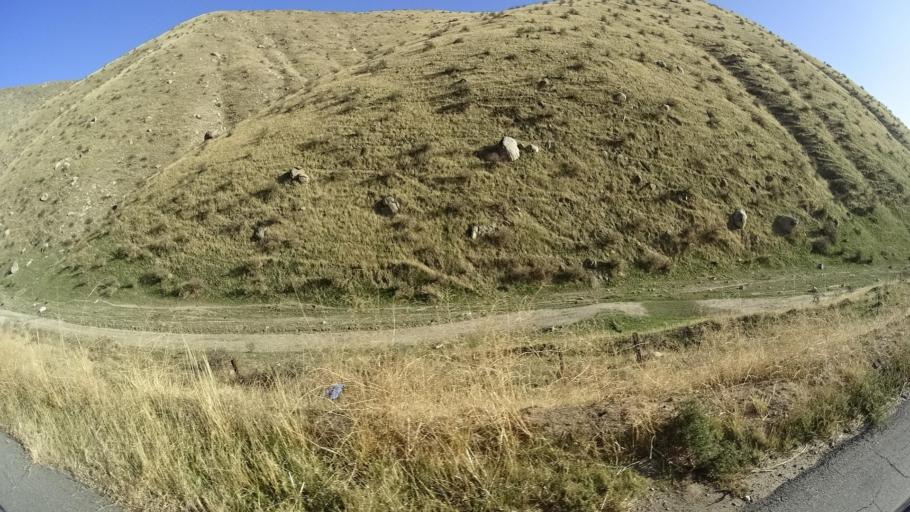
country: US
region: California
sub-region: Kern County
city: Bear Valley Springs
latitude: 35.2978
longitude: -118.6944
